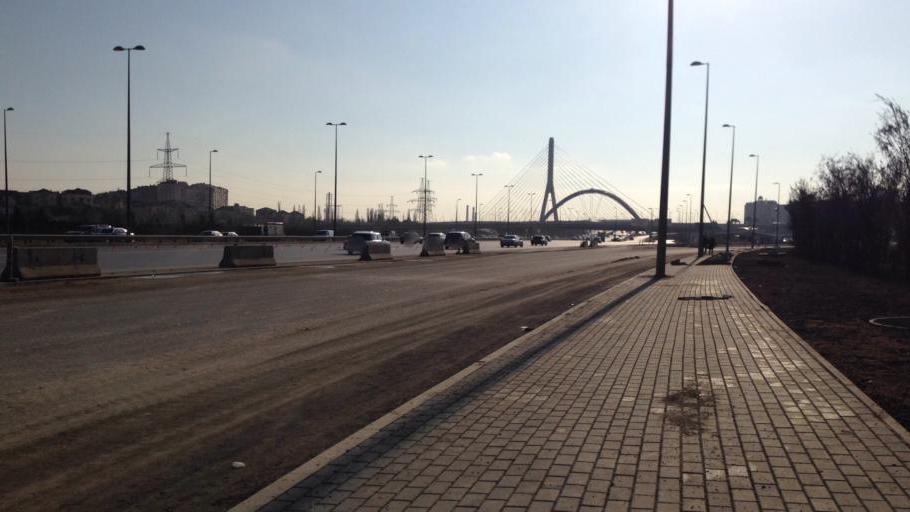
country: AZ
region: Baki
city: Sabuncu
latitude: 40.4293
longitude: 49.9246
